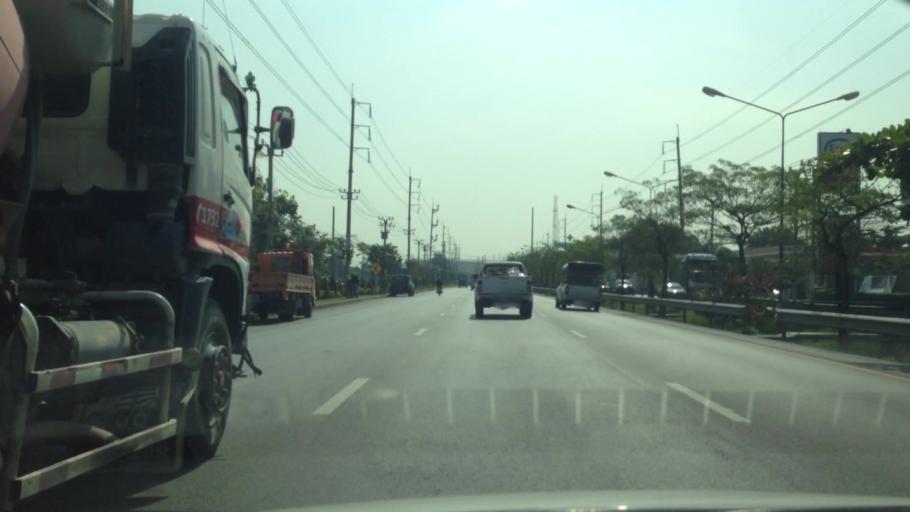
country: TH
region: Samut Prakan
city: Samut Prakan
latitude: 13.5285
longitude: 100.6360
